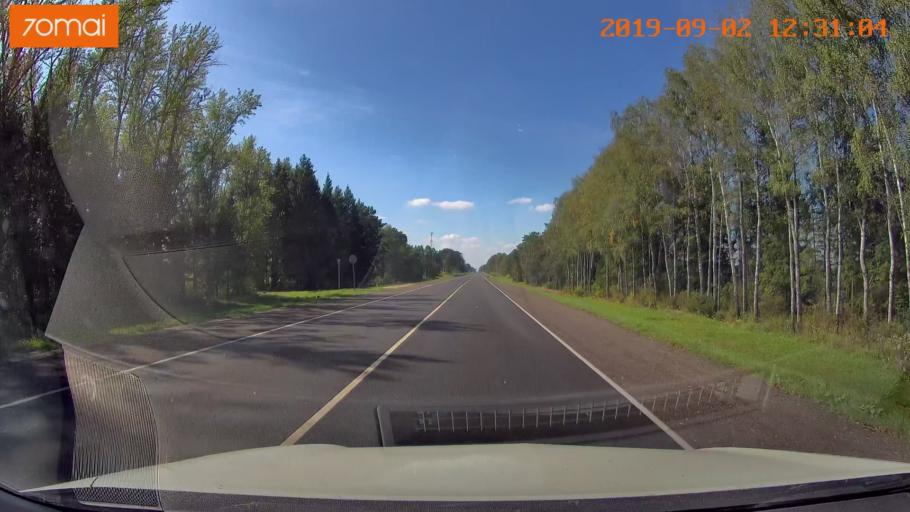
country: RU
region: Smolensk
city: Shumyachi
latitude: 53.8274
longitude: 32.4593
